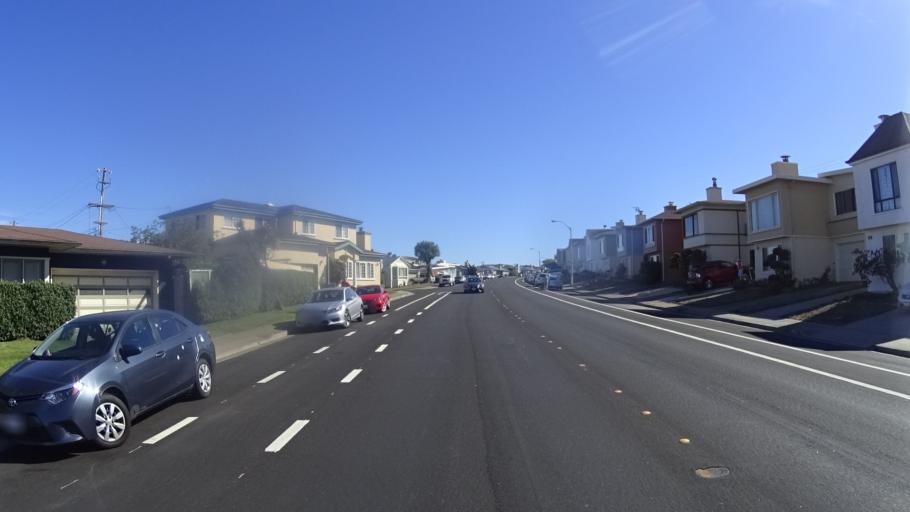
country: US
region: California
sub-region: San Mateo County
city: Broadmoor
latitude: 37.6885
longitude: -122.4883
